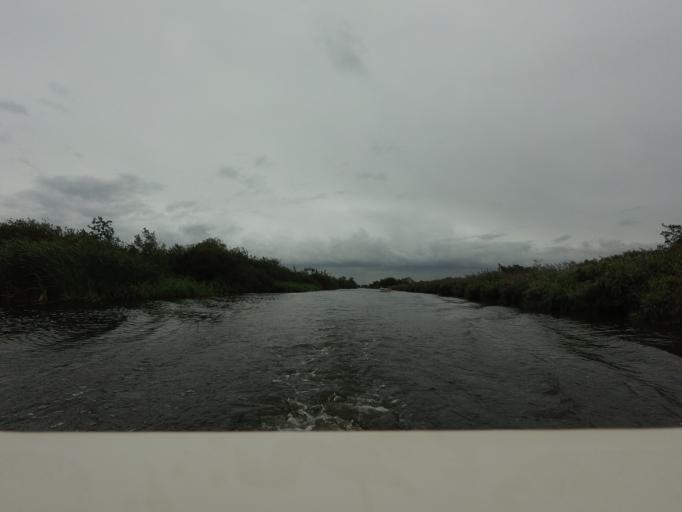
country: NL
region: Friesland
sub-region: Gemeente Boarnsterhim
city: Warten
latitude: 53.1209
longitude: 5.9292
